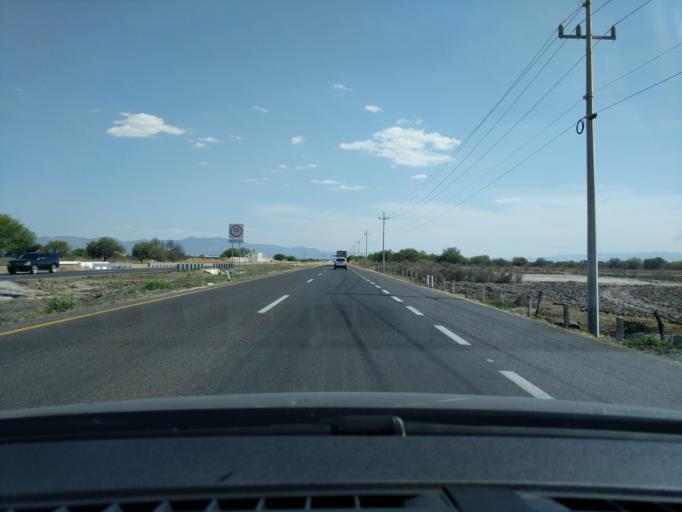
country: MX
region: Durango
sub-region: Durango
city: Jose Refugio Salcido
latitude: 24.0399
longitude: -104.5247
